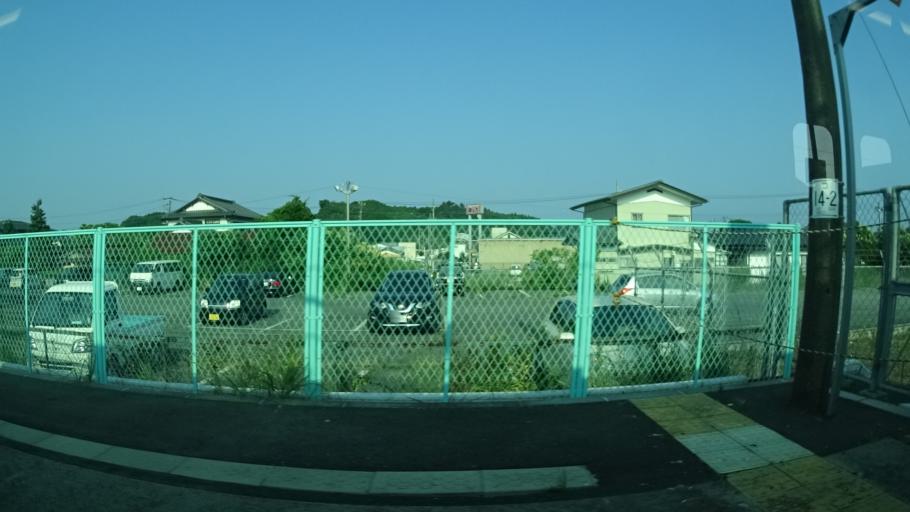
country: JP
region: Ibaraki
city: Kitaibaraki
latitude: 36.8458
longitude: 140.7782
